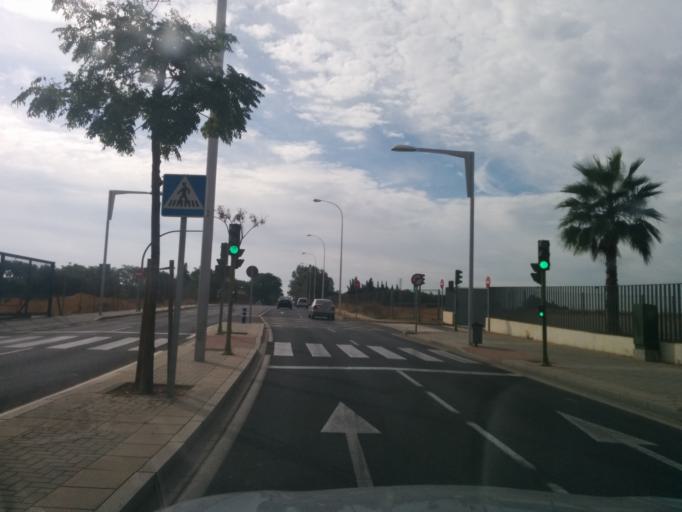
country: ES
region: Andalusia
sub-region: Provincia de Sevilla
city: Sevilla
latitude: 37.4029
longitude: -5.9342
